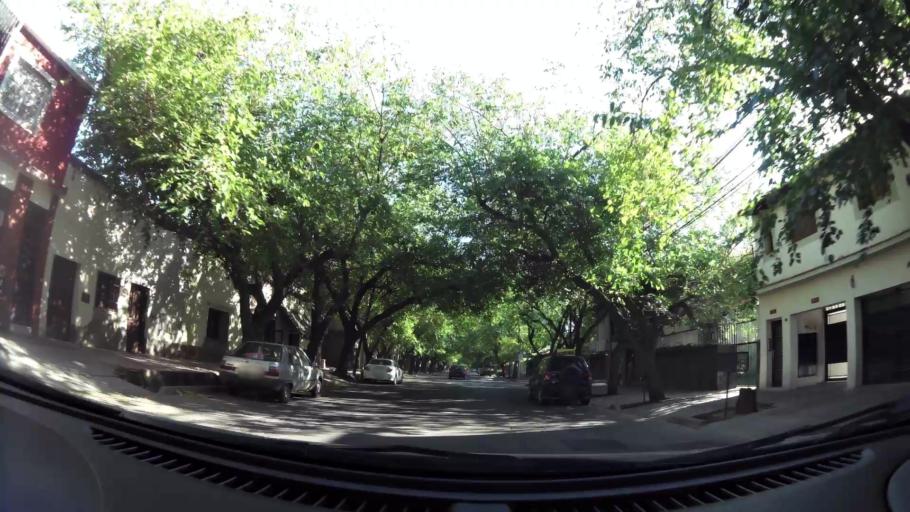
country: AR
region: Mendoza
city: Las Heras
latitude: -32.8717
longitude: -68.8371
